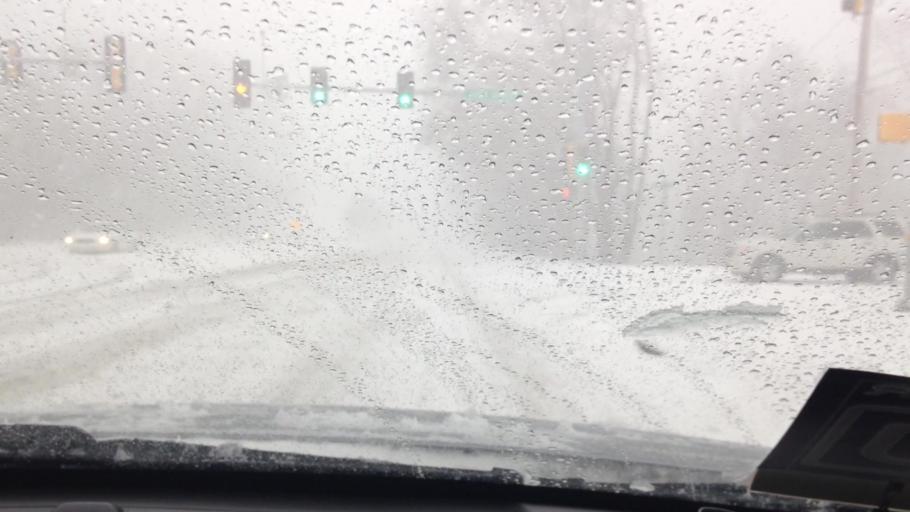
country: US
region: Kansas
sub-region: Johnson County
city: Shawnee
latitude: 39.1166
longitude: -94.7204
